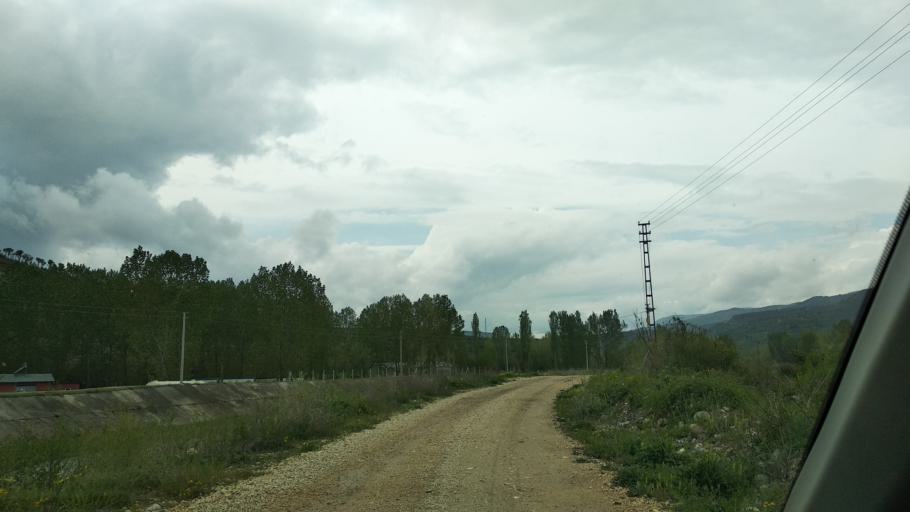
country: TR
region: Bolu
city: Seben
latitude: 40.4081
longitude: 31.5649
